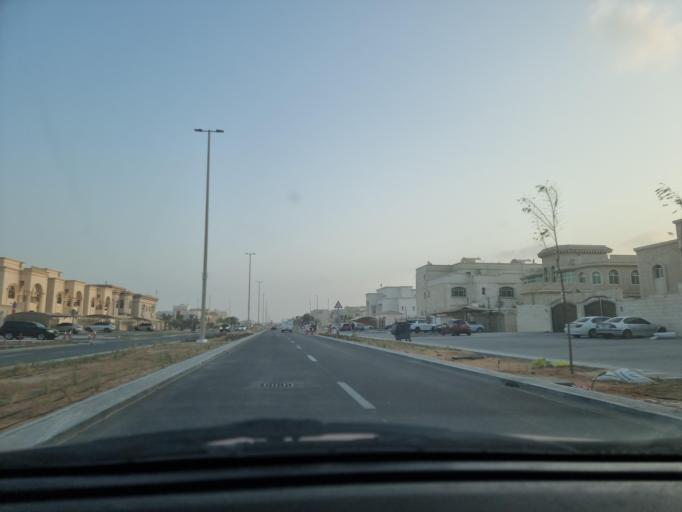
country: AE
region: Abu Dhabi
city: Abu Dhabi
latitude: 24.4235
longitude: 54.5740
